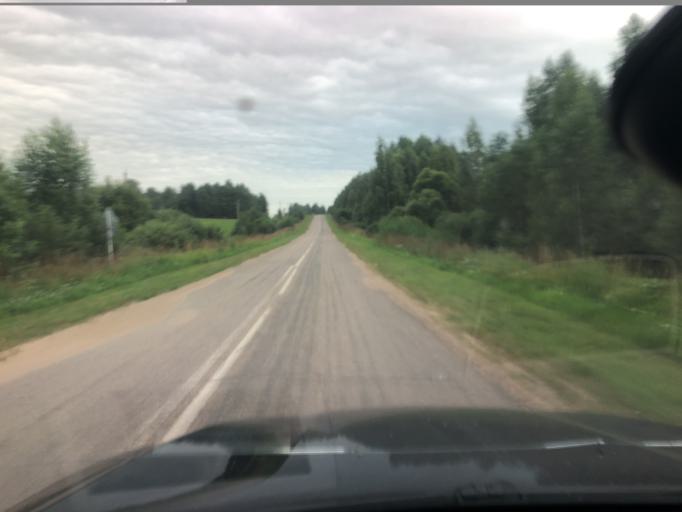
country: RU
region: Jaroslavl
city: Pereslavl'-Zalesskiy
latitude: 57.0281
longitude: 38.9175
